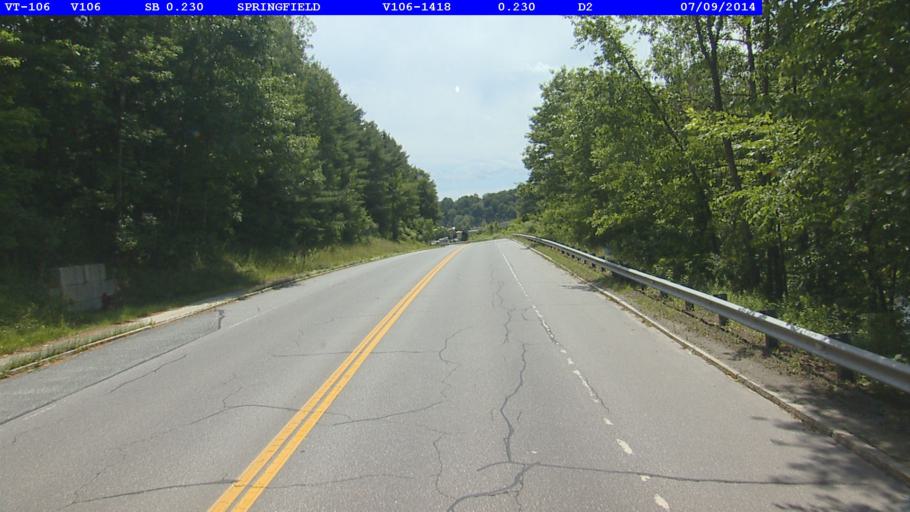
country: US
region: Vermont
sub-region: Windsor County
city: Springfield
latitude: 43.3064
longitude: -72.4945
